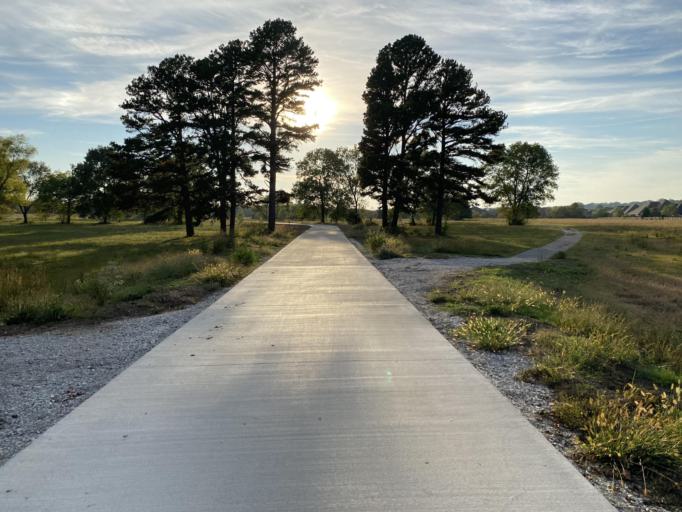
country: US
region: Arkansas
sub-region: Washington County
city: Johnson
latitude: 36.1053
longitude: -94.1951
